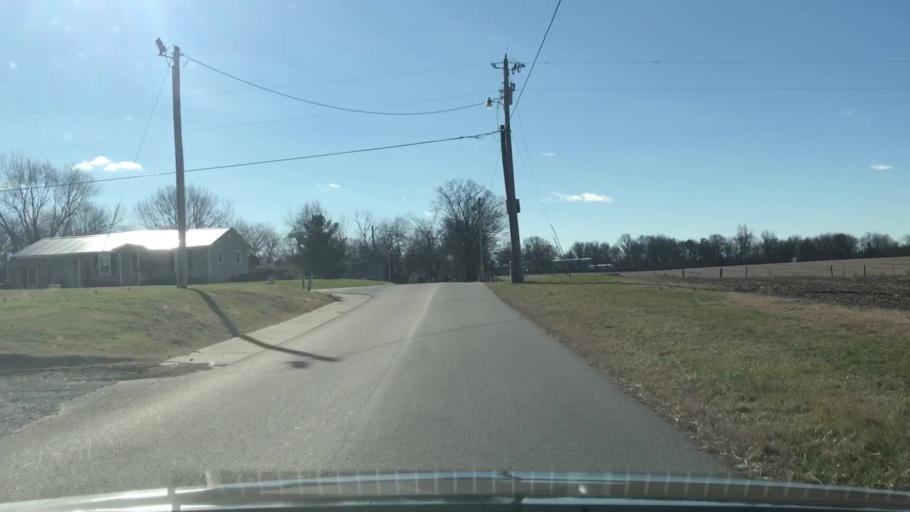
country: US
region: Kentucky
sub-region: Edmonson County
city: Brownsville
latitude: 37.0556
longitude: -86.2110
